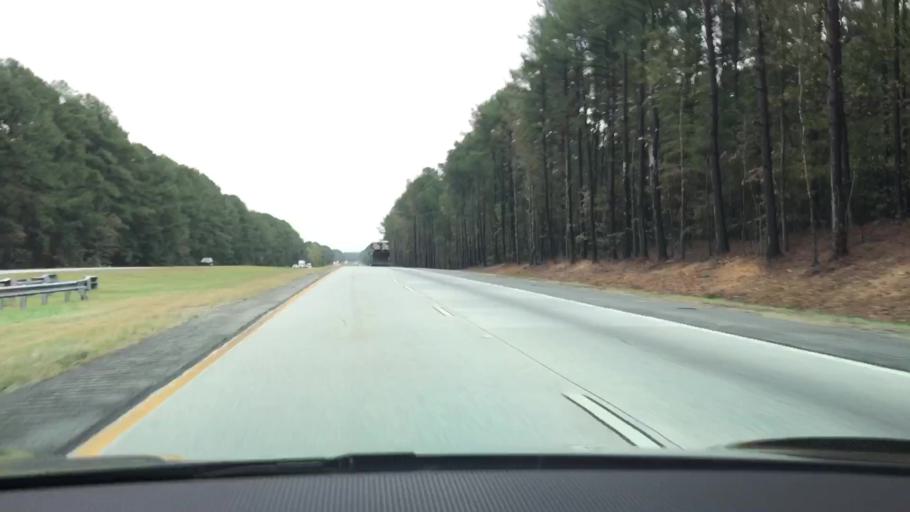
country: US
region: Georgia
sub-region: Taliaferro County
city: Crawfordville
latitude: 33.5115
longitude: -82.8469
